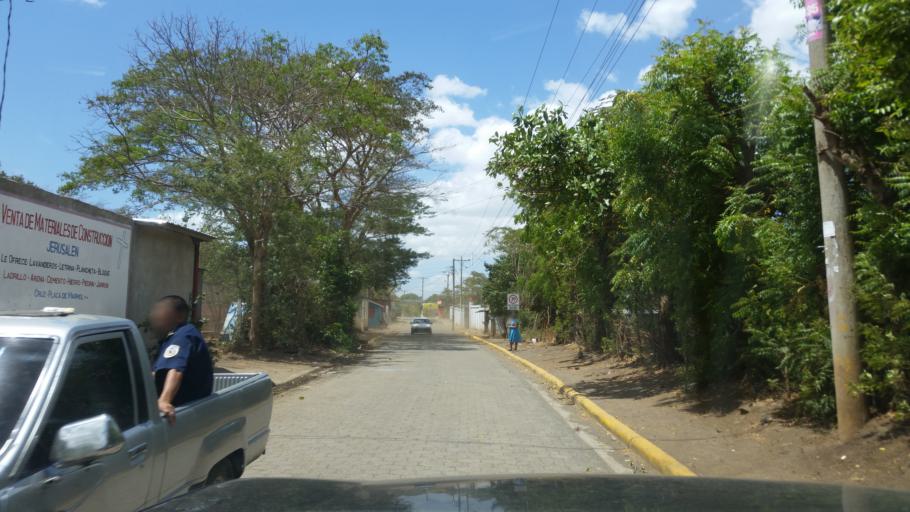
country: NI
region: Managua
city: Managua
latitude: 12.1088
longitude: -86.2129
